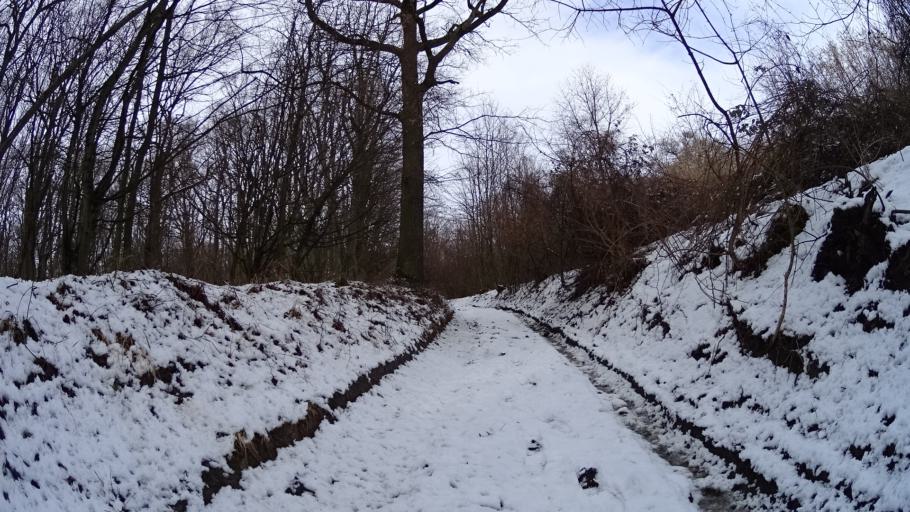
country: AT
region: Lower Austria
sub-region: Politischer Bezirk Korneuburg
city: Niederhollabrunn
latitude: 48.4137
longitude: 16.3022
